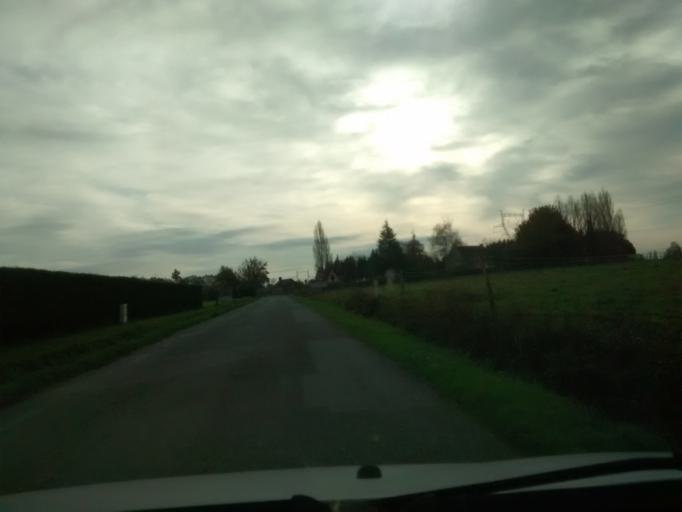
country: FR
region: Brittany
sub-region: Departement d'Ille-et-Vilaine
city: Noyal-sur-Vilaine
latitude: 48.0879
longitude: -1.5541
